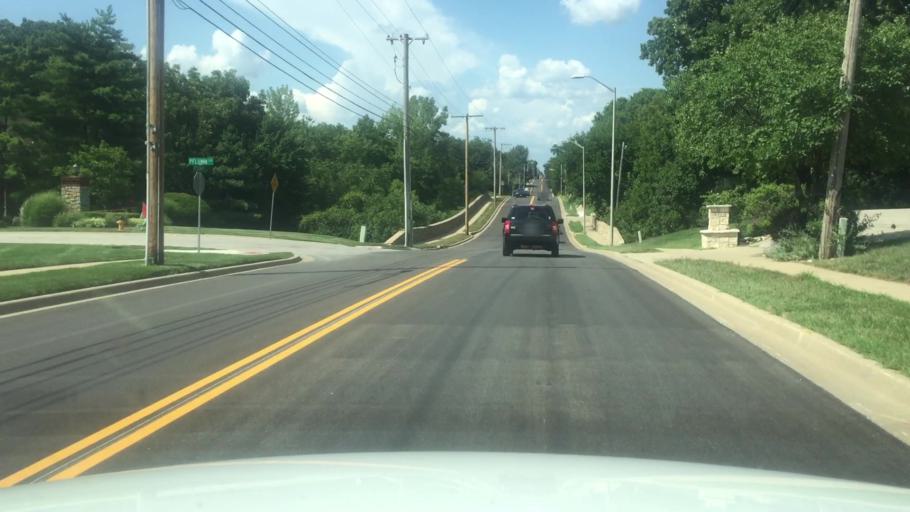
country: US
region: Kansas
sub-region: Johnson County
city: Lenexa
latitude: 38.9752
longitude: -94.7422
